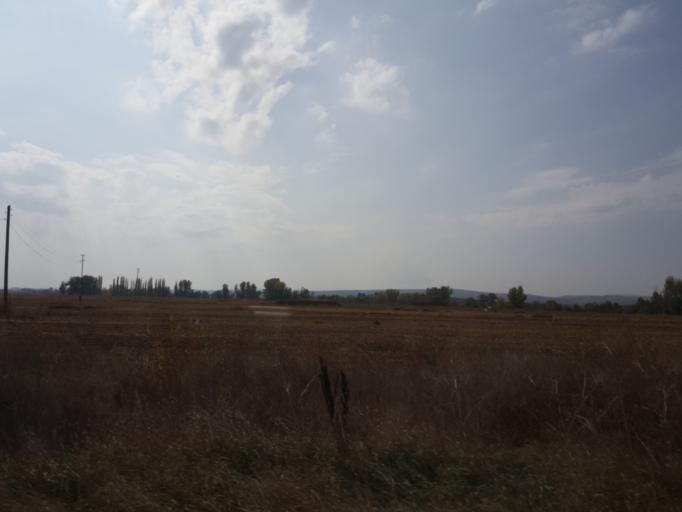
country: TR
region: Corum
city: Alaca
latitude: 40.1751
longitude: 34.8977
